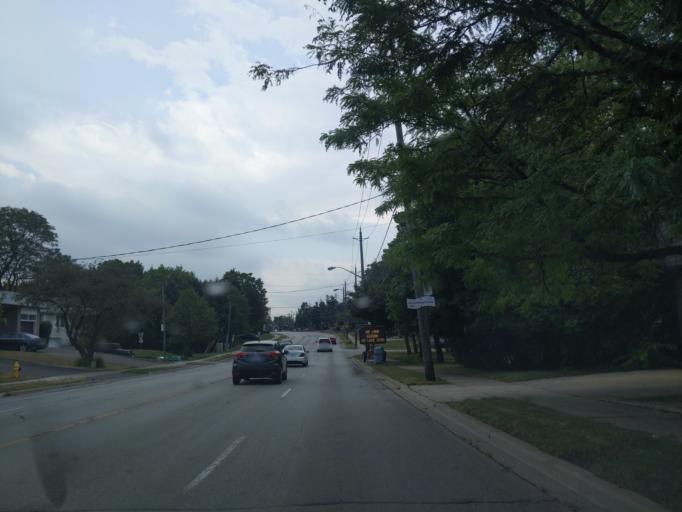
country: CA
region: Ontario
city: North York
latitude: 43.7874
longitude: -79.4100
